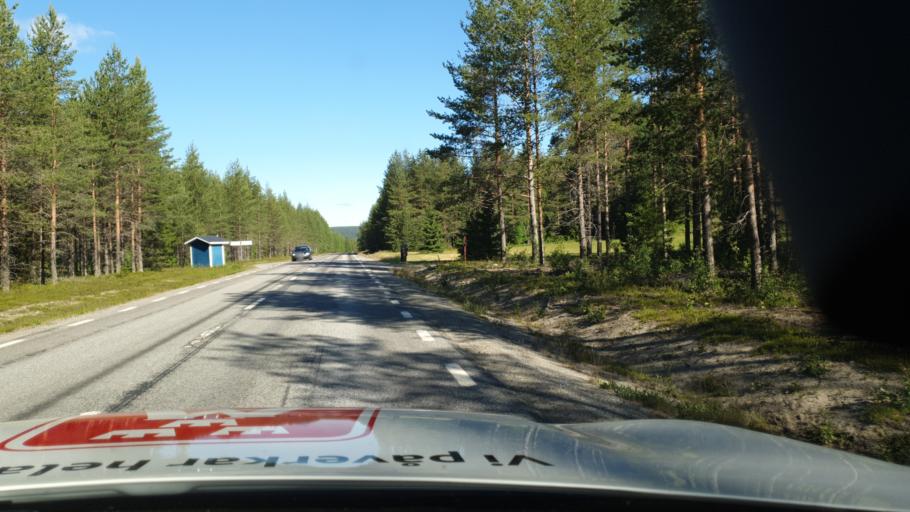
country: SE
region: Vaesterbotten
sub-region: Vindelns Kommun
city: Vindeln
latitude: 64.2521
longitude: 19.6383
